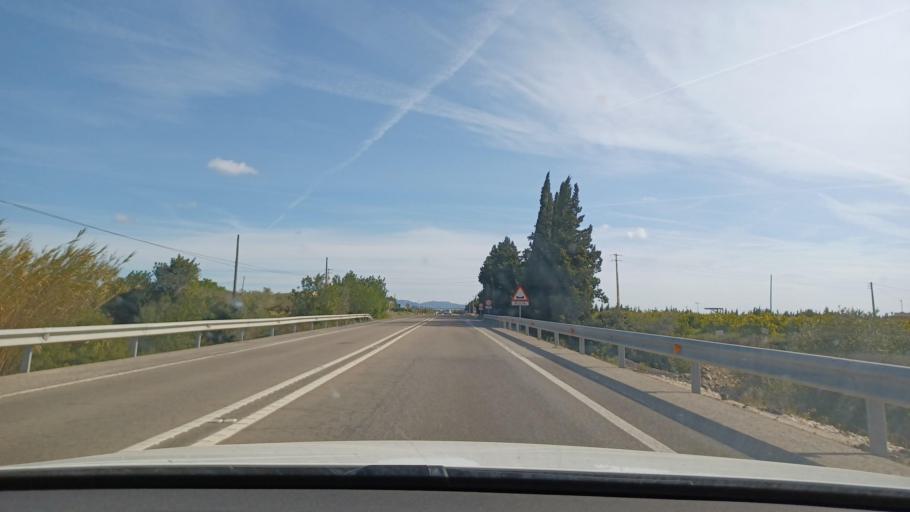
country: ES
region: Catalonia
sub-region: Provincia de Tarragona
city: Camarles
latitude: 40.7855
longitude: 0.6692
